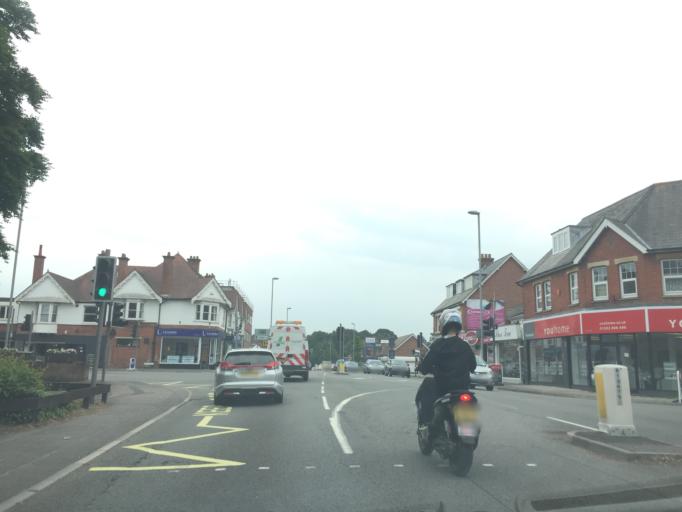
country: GB
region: England
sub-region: Dorset
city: Ferndown
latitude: 50.8014
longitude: -1.8900
